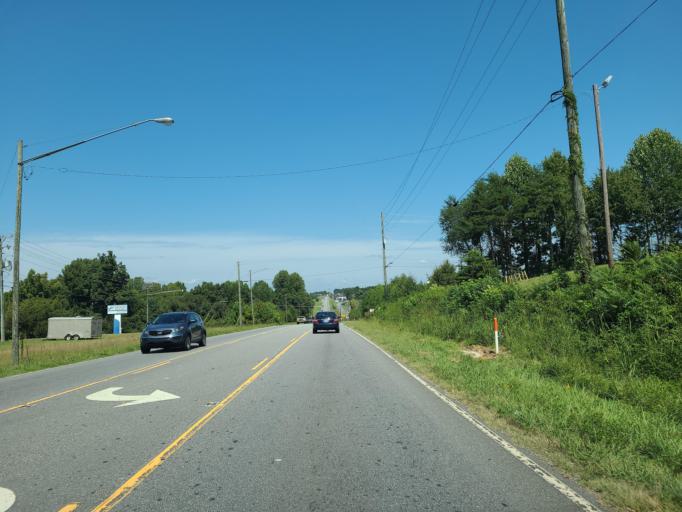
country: US
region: North Carolina
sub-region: Lincoln County
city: Lincolnton
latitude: 35.4816
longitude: -81.2420
